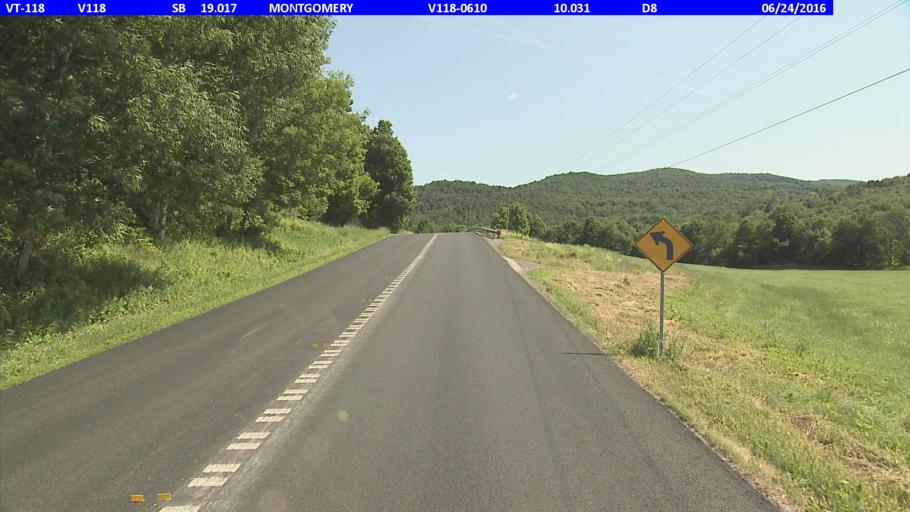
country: US
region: Vermont
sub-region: Franklin County
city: Richford
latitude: 44.9145
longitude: -72.6688
